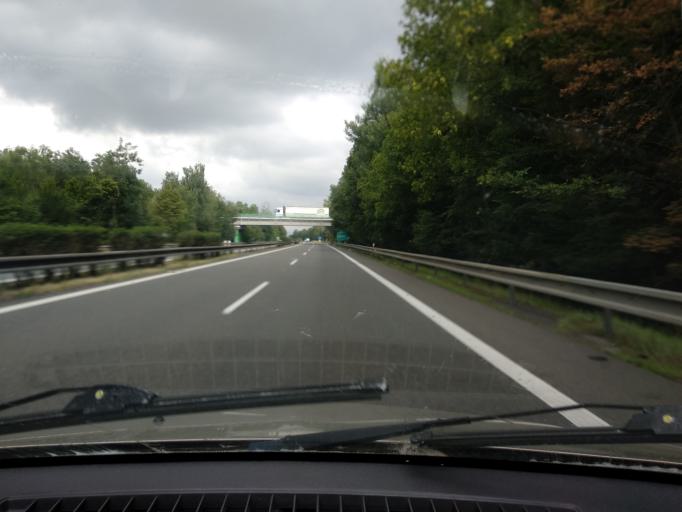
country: CZ
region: Olomoucky
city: Bila Lhota
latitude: 49.7098
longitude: 17.0230
